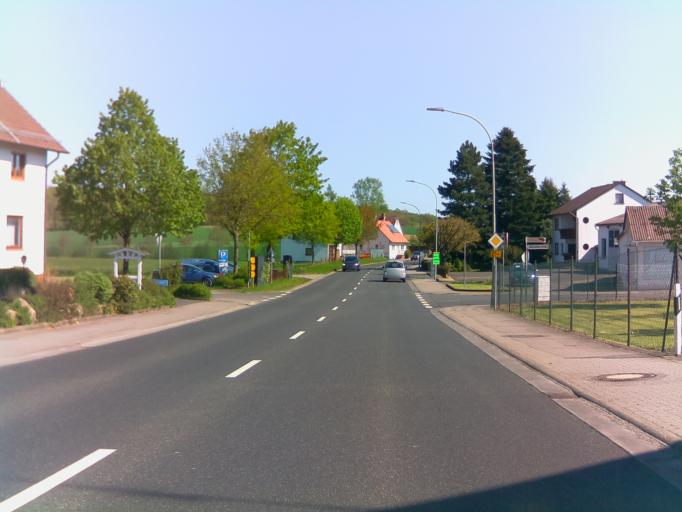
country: DE
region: Hesse
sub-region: Regierungsbezirk Giessen
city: Lauterbach
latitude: 50.6764
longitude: 9.3522
